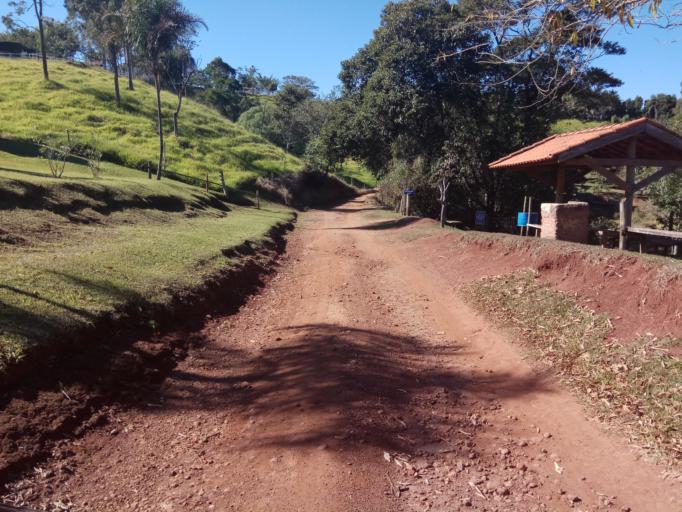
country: BR
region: Sao Paulo
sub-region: Itirapina
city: Itirapina
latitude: -22.3914
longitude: -47.8872
